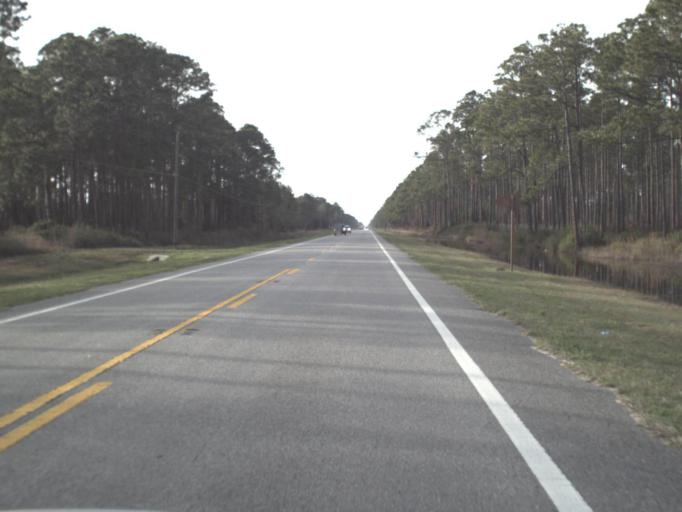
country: US
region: Florida
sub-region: Bay County
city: Mexico Beach
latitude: 30.0003
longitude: -85.4999
